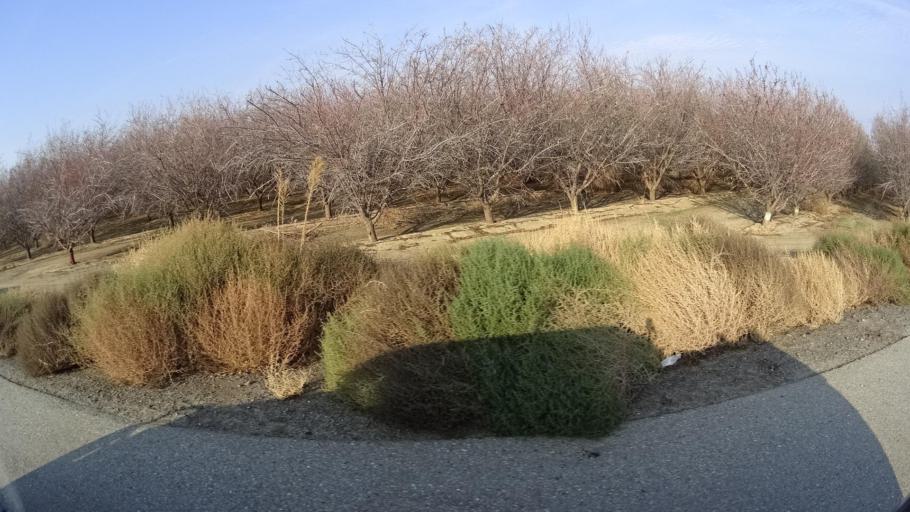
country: US
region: California
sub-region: Kern County
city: Lebec
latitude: 35.0266
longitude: -118.9293
